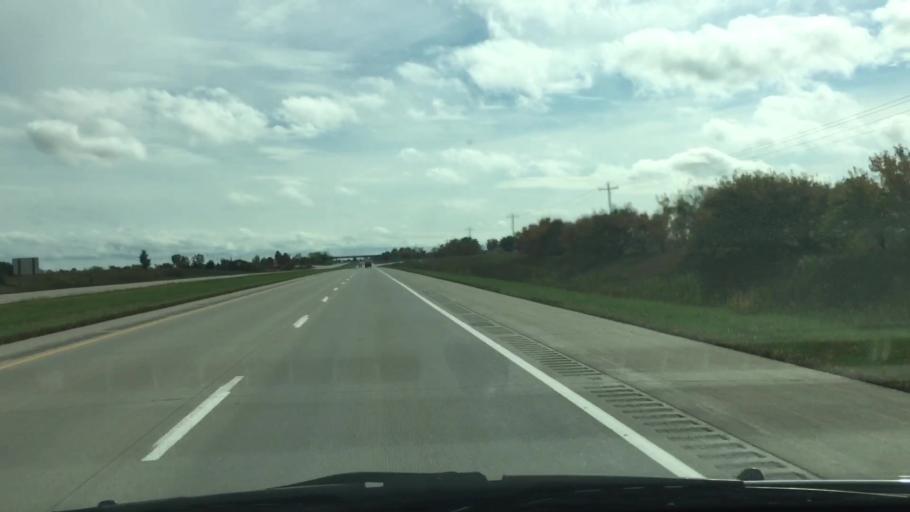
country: US
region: Iowa
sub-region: Clarke County
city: Osceola
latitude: 40.9812
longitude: -93.7978
